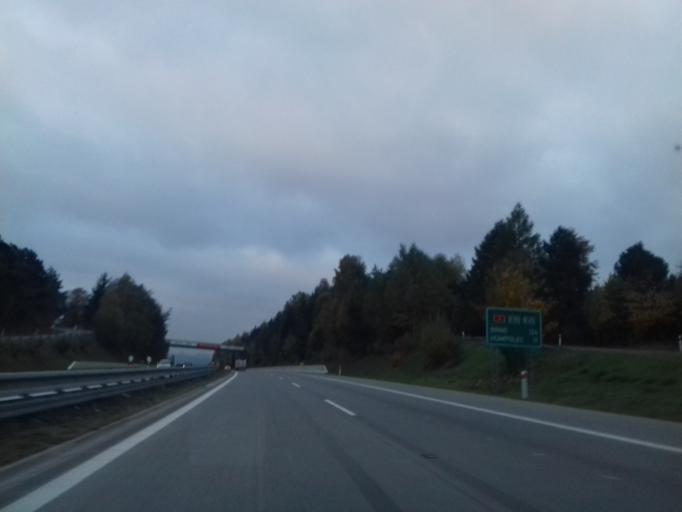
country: CZ
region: Vysocina
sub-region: Okres Pelhrimov
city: Zeliv
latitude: 49.6017
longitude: 15.1862
